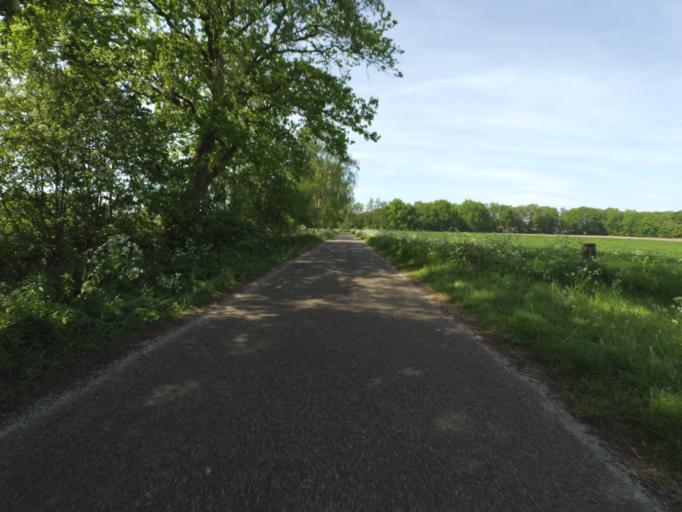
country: NL
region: Overijssel
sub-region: Gemeente Almelo
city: Almelo
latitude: 52.3490
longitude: 6.7143
